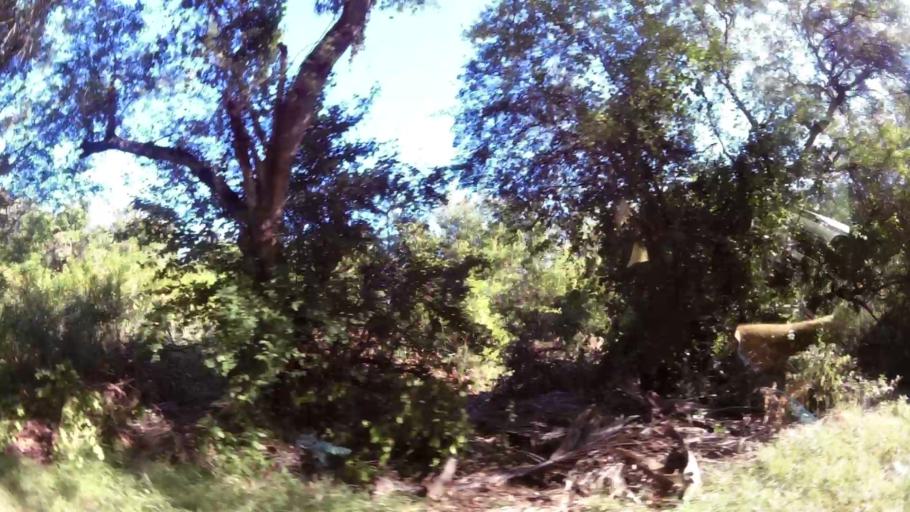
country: GT
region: Santa Rosa
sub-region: Municipio de Taxisco
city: Taxisco
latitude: 13.8887
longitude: -90.4776
